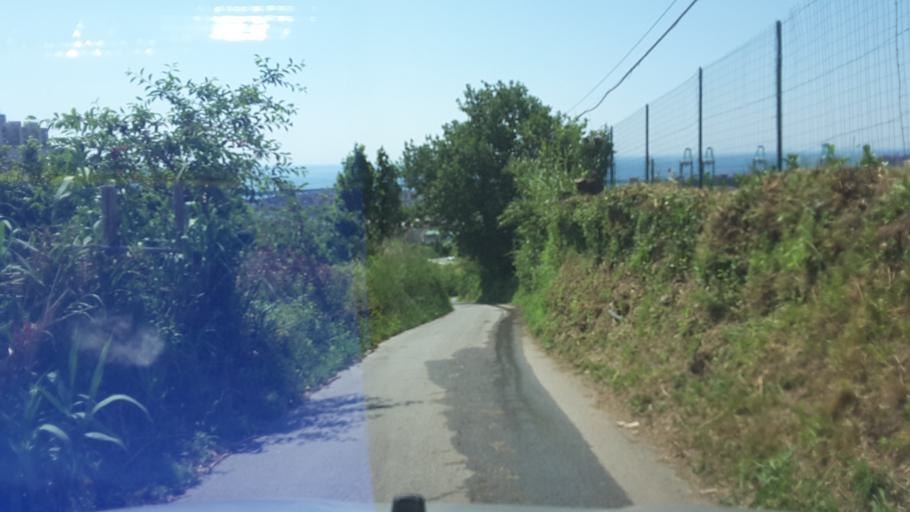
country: IT
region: Liguria
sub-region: Provincia di Genova
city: Mele
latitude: 44.4331
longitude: 8.7891
